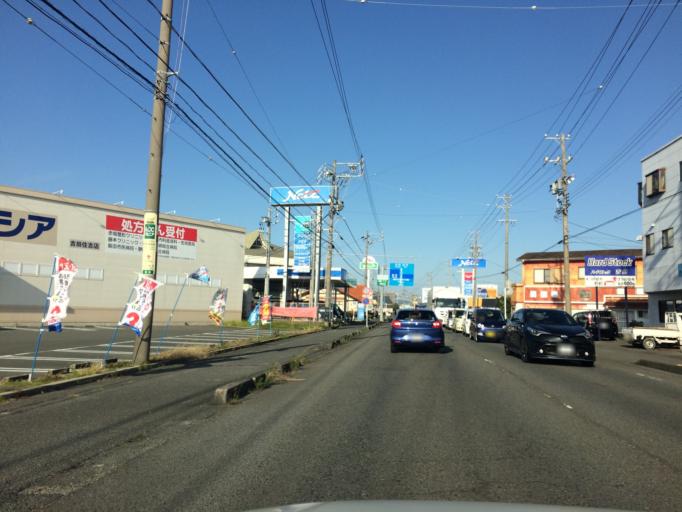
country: JP
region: Shizuoka
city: Shimada
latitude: 34.7652
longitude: 138.2487
